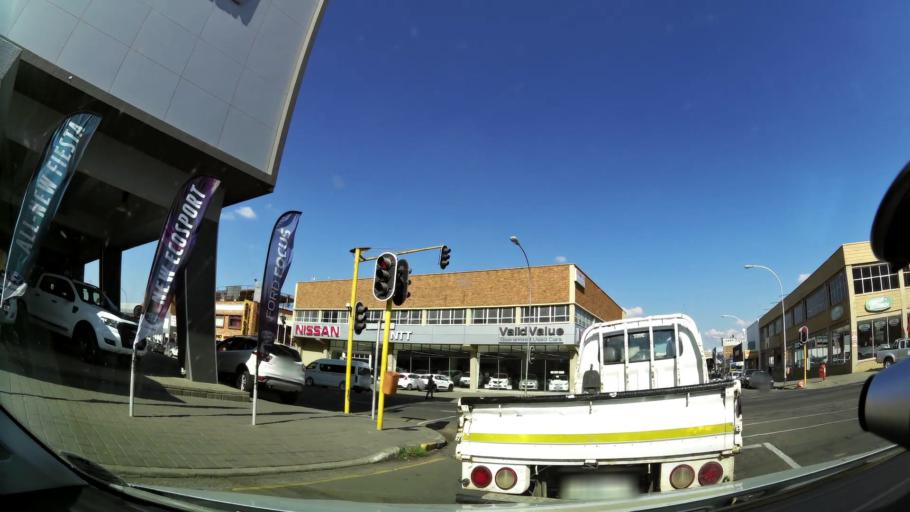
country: ZA
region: Orange Free State
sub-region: Mangaung Metropolitan Municipality
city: Bloemfontein
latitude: -29.1135
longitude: 26.2229
